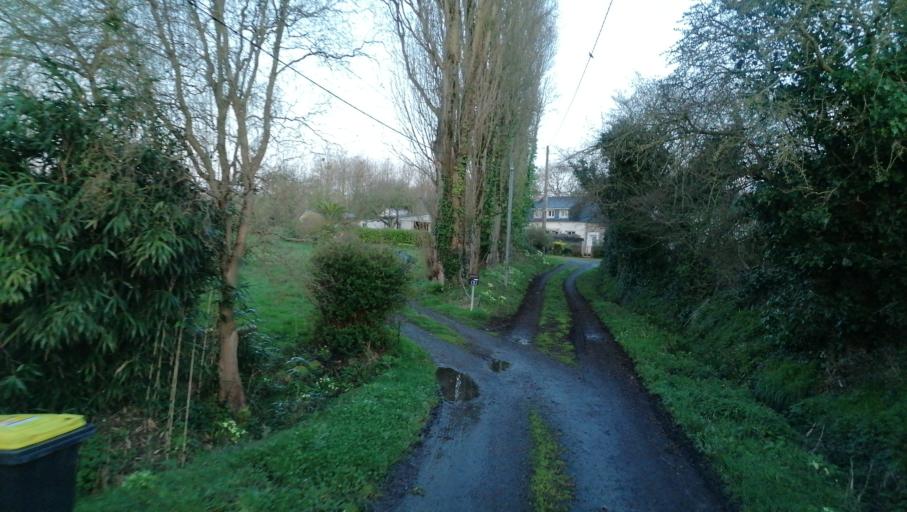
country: FR
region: Brittany
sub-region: Departement des Cotes-d'Armor
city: Plouha
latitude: 48.6675
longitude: -2.9391
